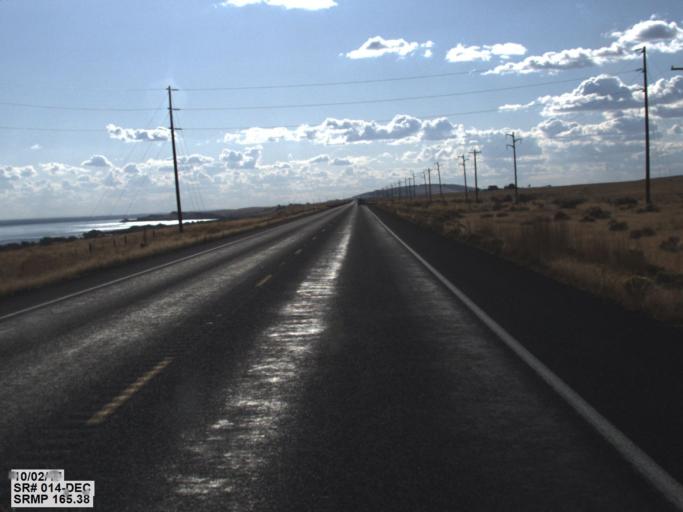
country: US
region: Oregon
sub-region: Morrow County
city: Boardman
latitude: 45.9236
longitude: -119.6368
